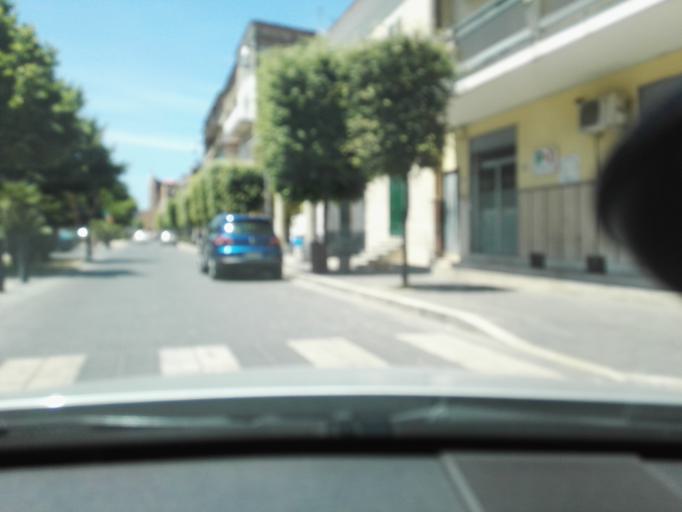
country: IT
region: Campania
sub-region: Provincia di Caserta
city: Casapesenna
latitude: 40.9918
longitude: 14.1381
